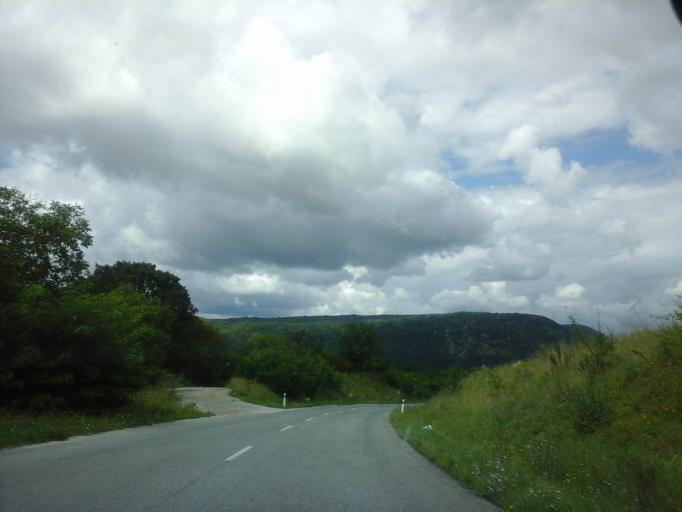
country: SK
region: Kosicky
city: Roznava
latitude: 48.5366
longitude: 20.4093
